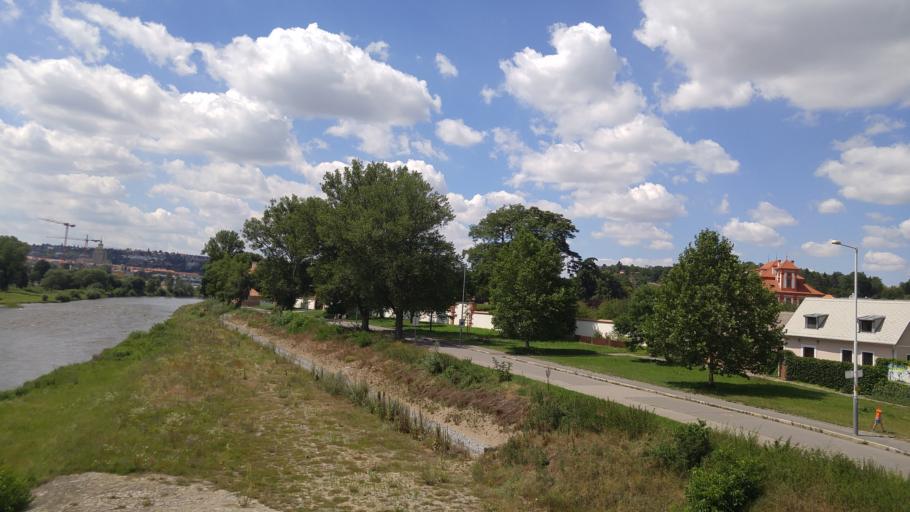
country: CZ
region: Praha
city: Prague
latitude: 50.1150
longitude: 14.4166
